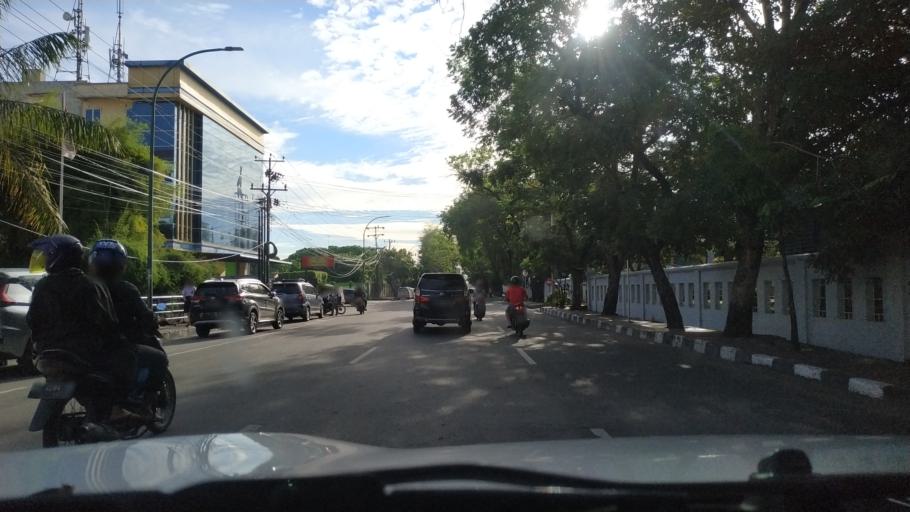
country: ID
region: North Sumatra
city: Medan
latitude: 3.5987
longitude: 98.6882
